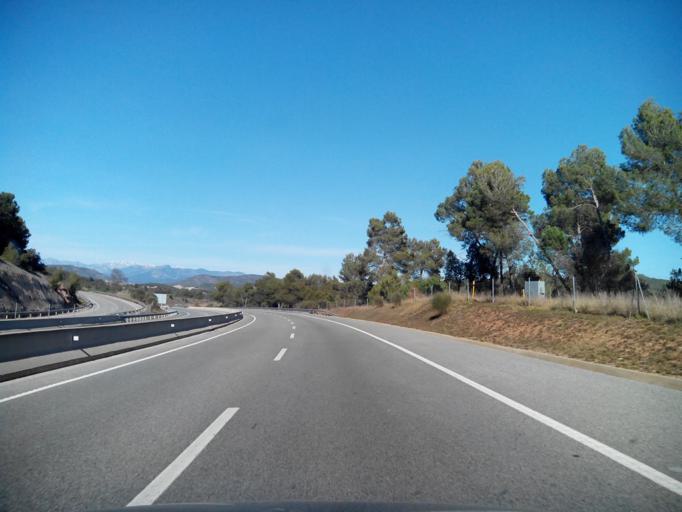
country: ES
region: Catalonia
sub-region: Provincia de Barcelona
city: Navas
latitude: 41.9103
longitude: 1.8814
